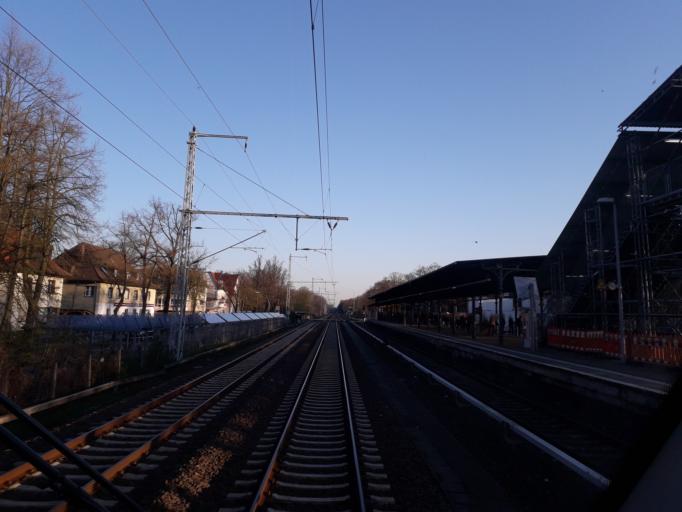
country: DE
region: Brandenburg
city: Zeuthen
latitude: 52.3709
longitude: 13.6154
